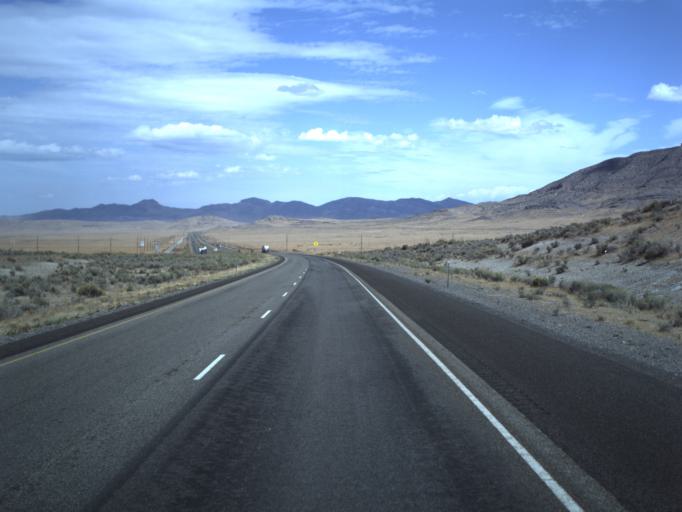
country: US
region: Utah
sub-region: Tooele County
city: Grantsville
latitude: 40.7686
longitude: -112.9838
